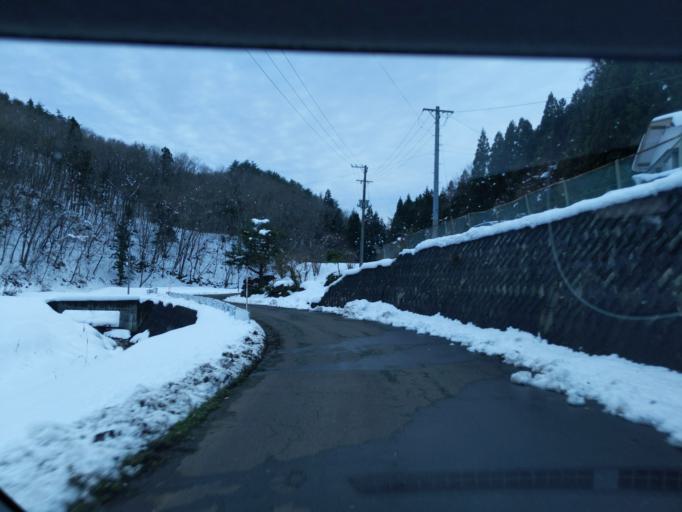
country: JP
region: Iwate
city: Mizusawa
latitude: 39.0406
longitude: 141.0102
